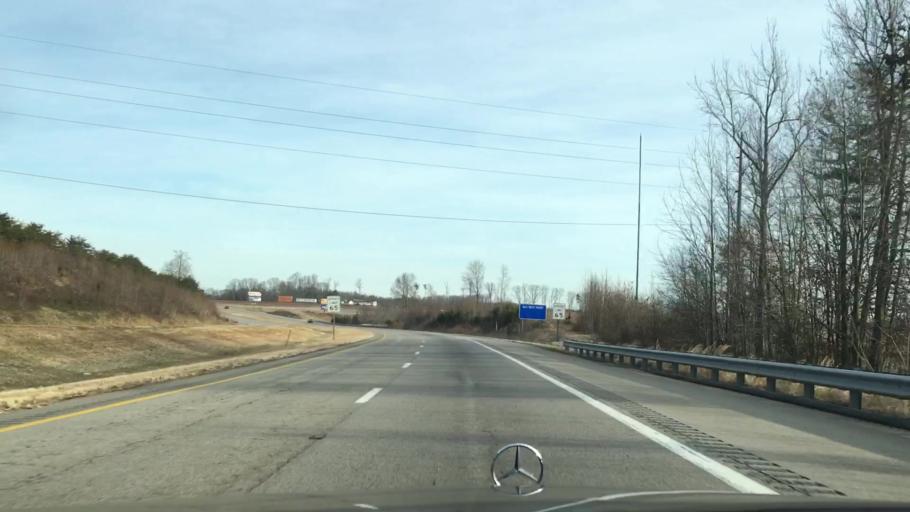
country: US
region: Virginia
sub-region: Pittsylvania County
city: Mount Hermon
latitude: 36.6885
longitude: -79.3614
